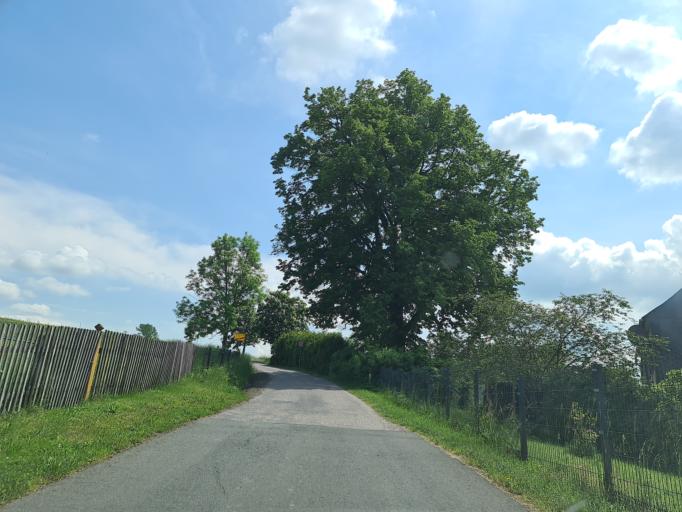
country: DE
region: Saxony
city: Stollberg
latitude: 50.6762
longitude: 12.7430
